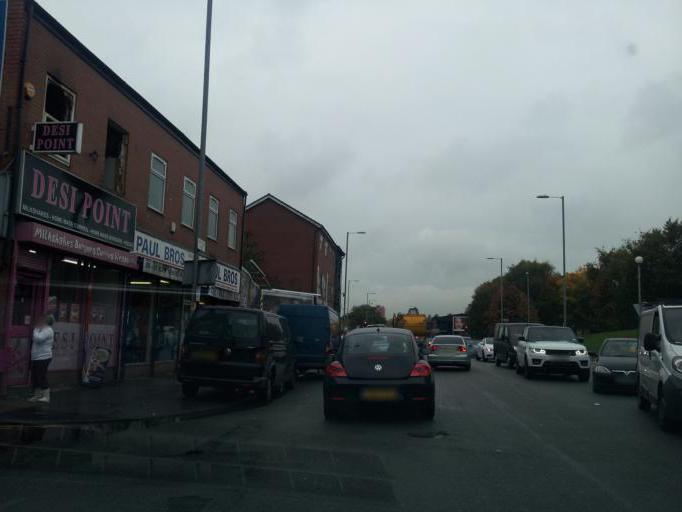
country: GB
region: England
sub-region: Manchester
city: Cheetham Hill
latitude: 53.4942
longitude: -2.2506
